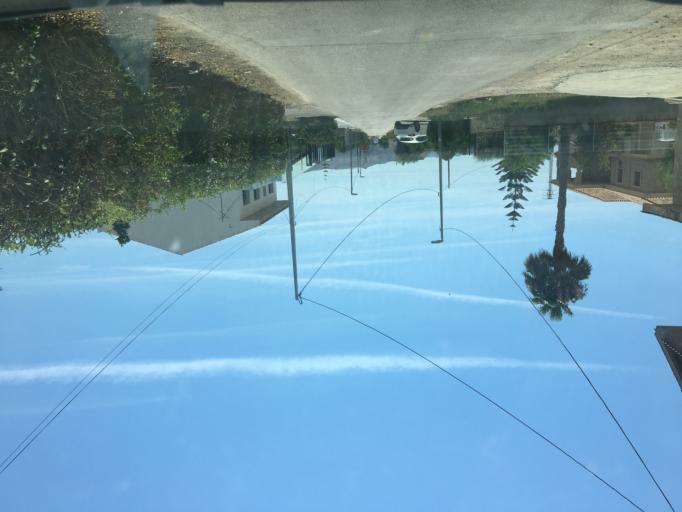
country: ES
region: Murcia
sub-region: Murcia
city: Santomera
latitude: 38.0301
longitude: -1.0637
